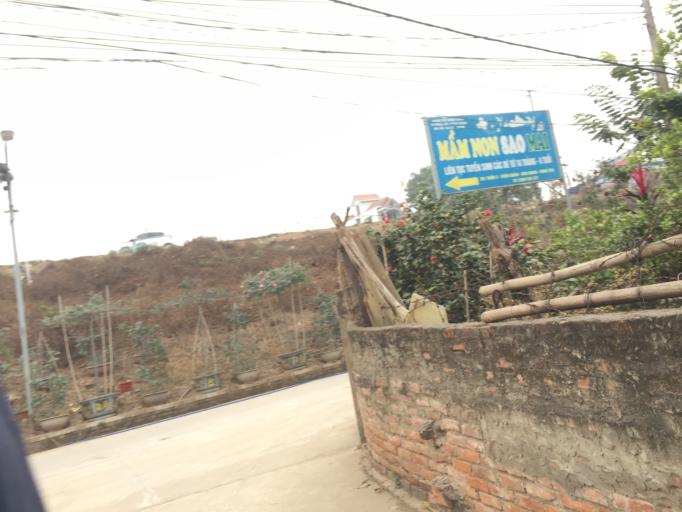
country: VN
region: Hung Yen
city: Van Giang
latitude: 20.9700
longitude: 105.9197
